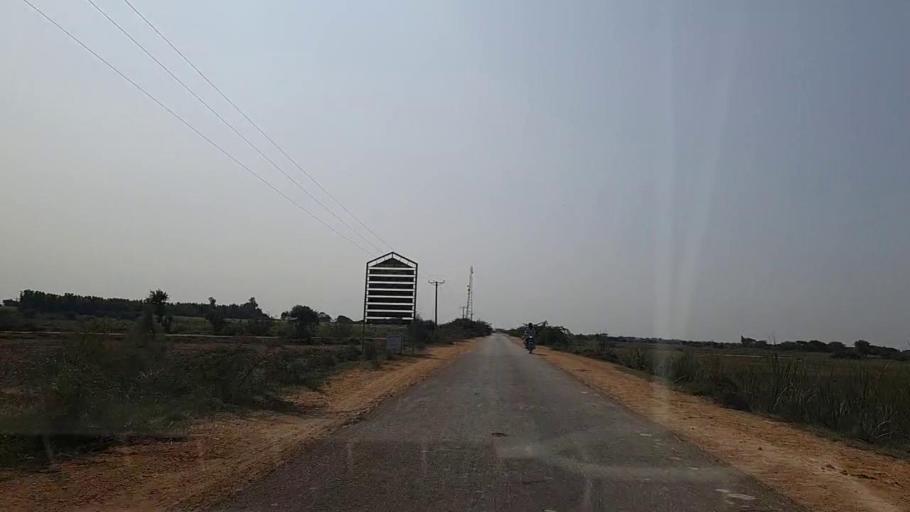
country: PK
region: Sindh
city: Chuhar Jamali
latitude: 24.2884
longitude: 67.9247
